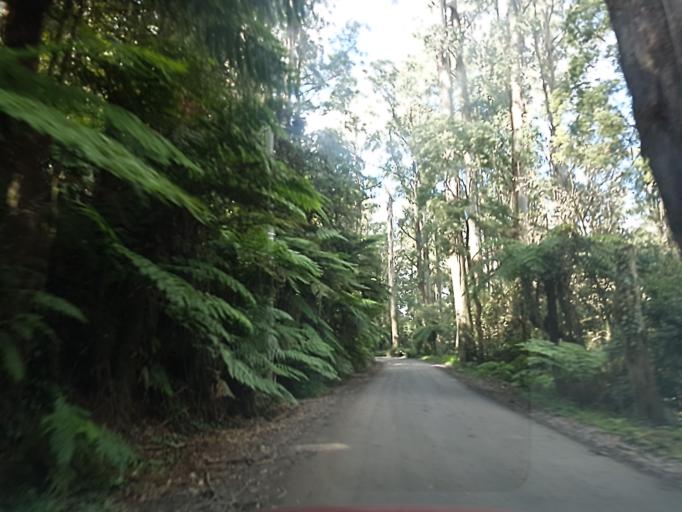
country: AU
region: Victoria
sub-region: Yarra Ranges
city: Kallista
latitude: -37.8789
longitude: 145.3788
